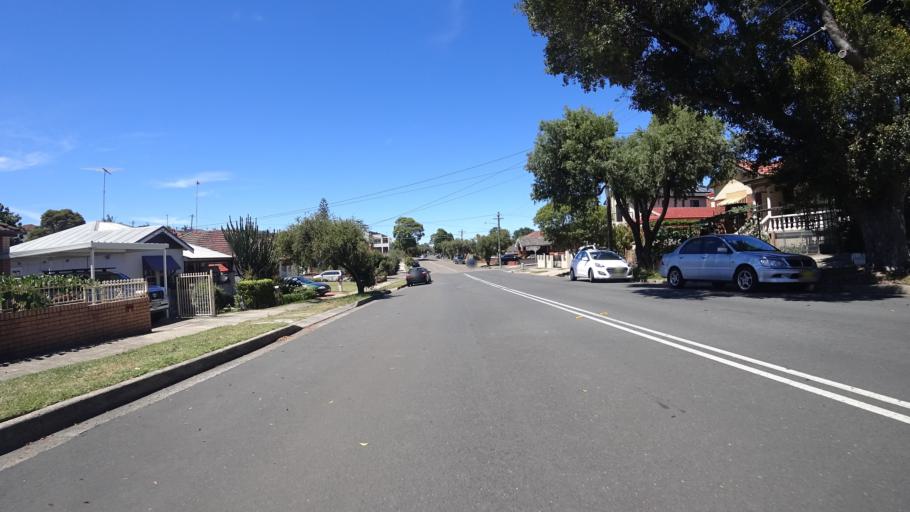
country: AU
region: New South Wales
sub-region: Rockdale
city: Bexley
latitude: -33.9625
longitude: 151.1251
